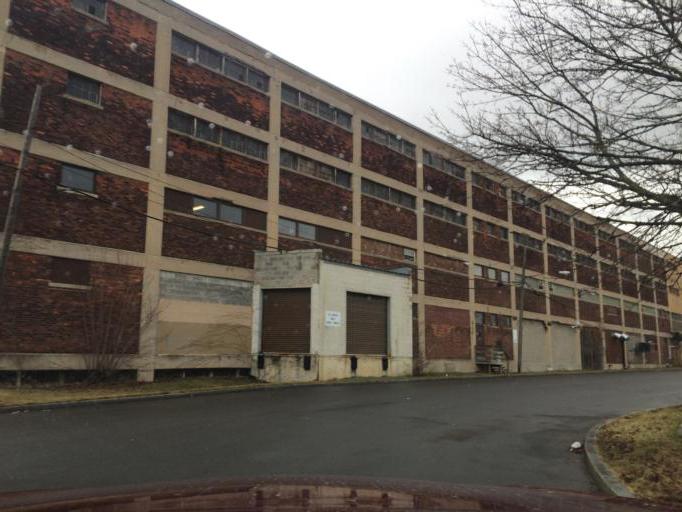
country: US
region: New York
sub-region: Oneida County
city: Utica
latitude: 43.1061
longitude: -75.2284
